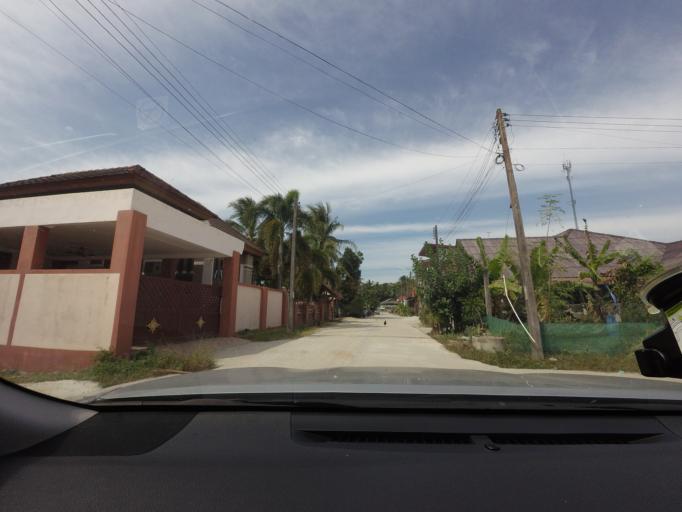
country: TH
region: Narathiwat
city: Narathiwat
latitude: 6.4158
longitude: 101.8466
